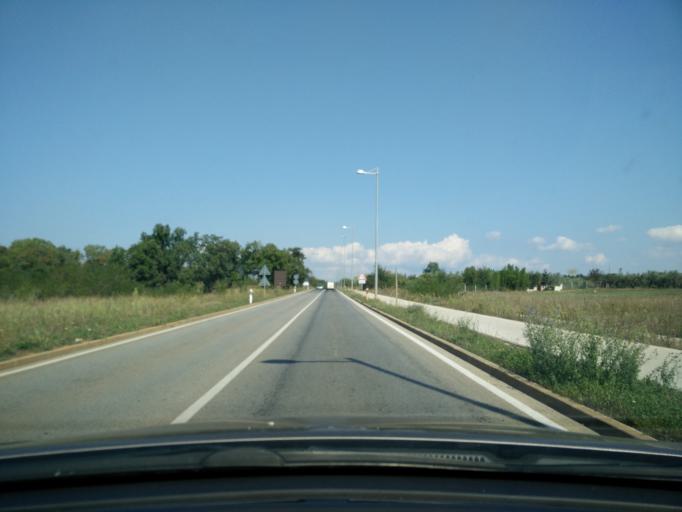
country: HR
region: Istarska
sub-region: Grad Porec
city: Porec
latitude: 45.2540
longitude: 13.6220
